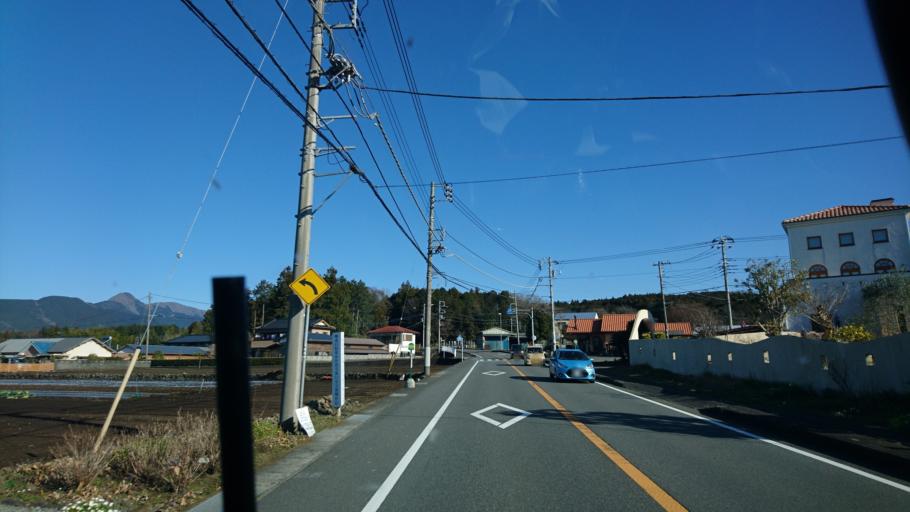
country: JP
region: Shizuoka
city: Fujinomiya
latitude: 35.2613
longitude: 138.6062
